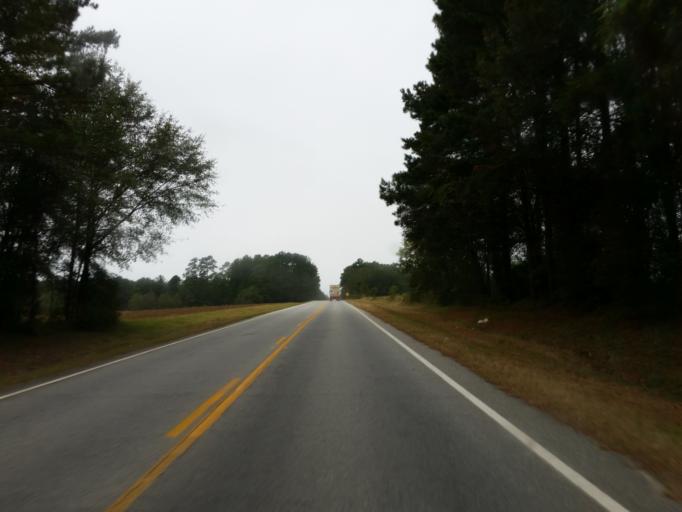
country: US
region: Georgia
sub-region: Berrien County
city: Ray City
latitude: 31.1068
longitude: -83.2864
